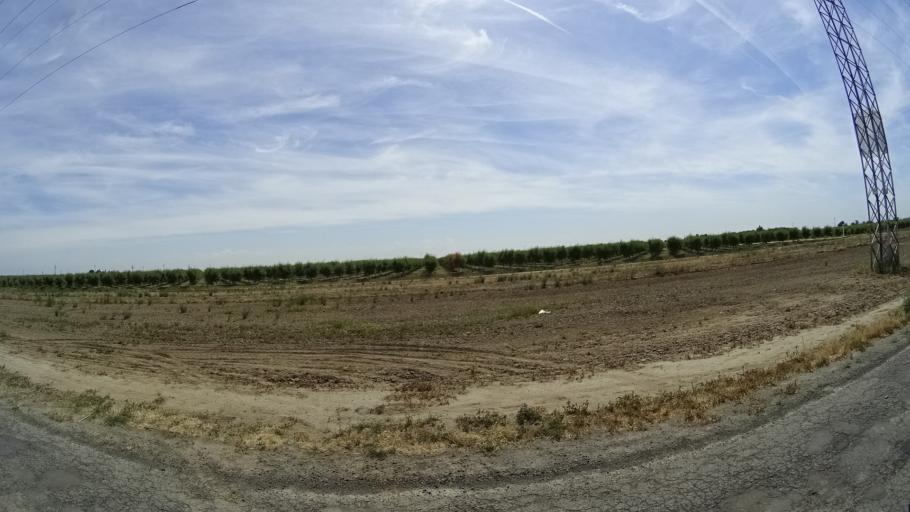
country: US
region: California
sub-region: Kings County
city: Hanford
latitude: 36.3473
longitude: -119.5921
